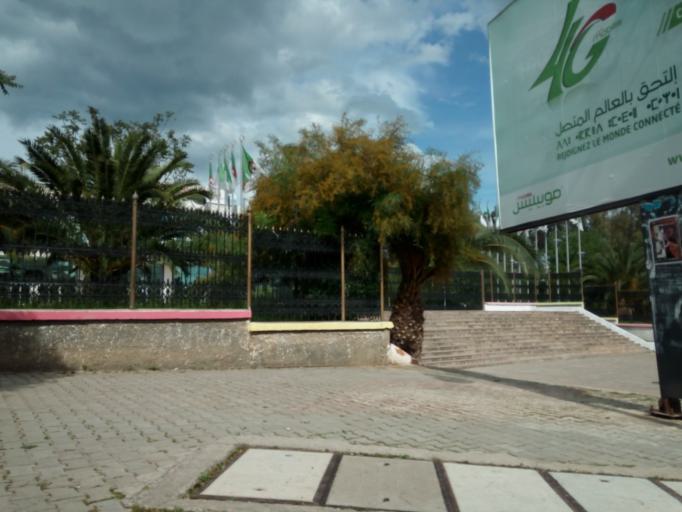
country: DZ
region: Constantine
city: Constantine
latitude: 36.3511
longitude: 6.6085
